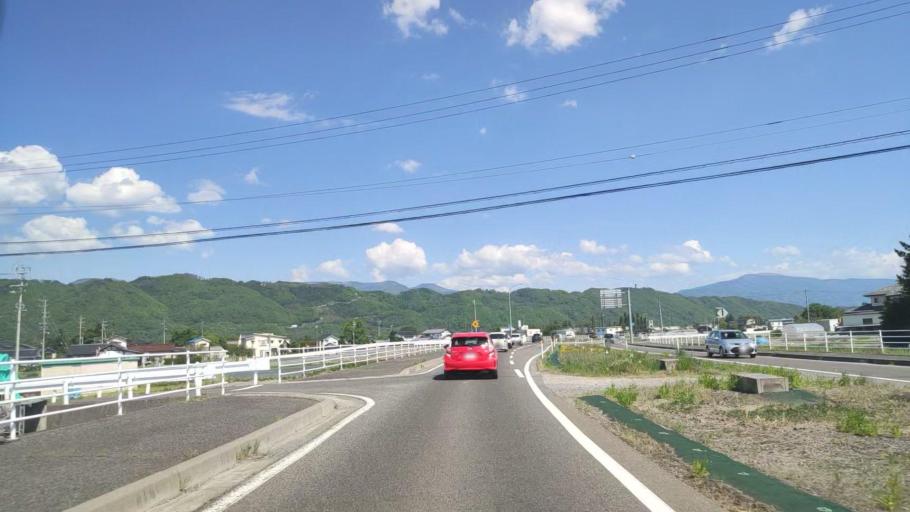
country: JP
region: Nagano
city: Toyoshina
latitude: 36.2792
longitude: 137.9224
